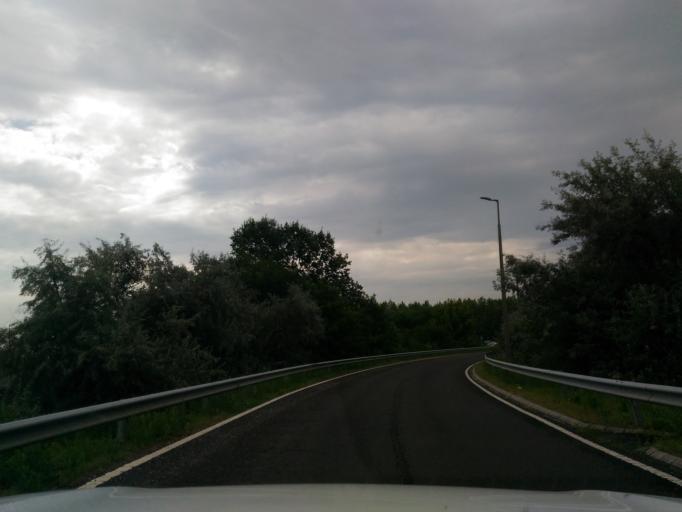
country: HU
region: Jasz-Nagykun-Szolnok
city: Toszeg
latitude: 47.1456
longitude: 20.1587
